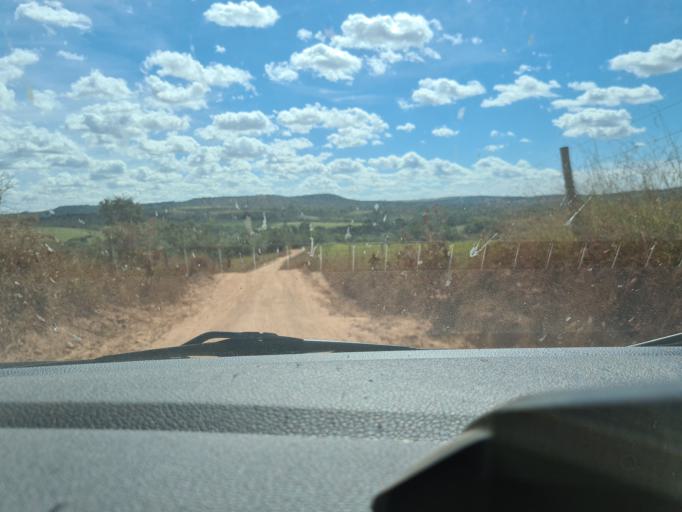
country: BR
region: Goias
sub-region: Silvania
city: Silvania
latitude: -16.5388
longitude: -48.5796
